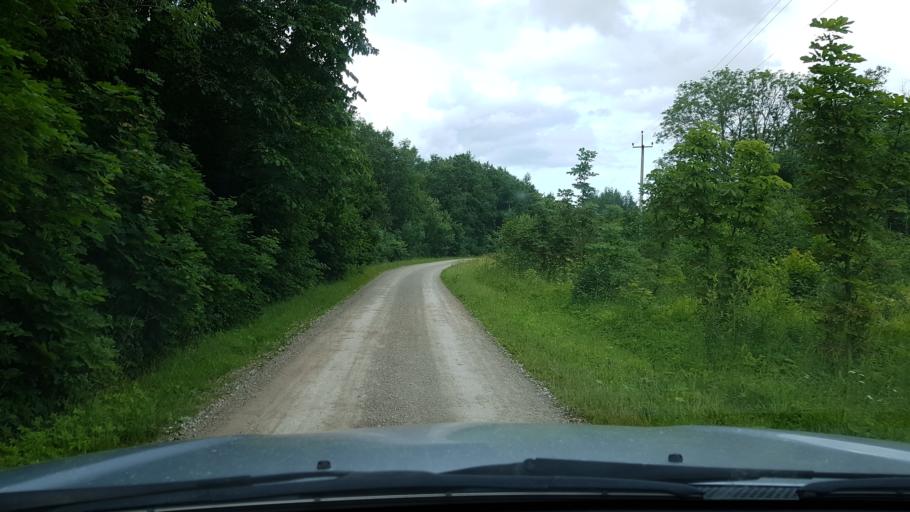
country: EE
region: Ida-Virumaa
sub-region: Narva-Joesuu linn
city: Narva-Joesuu
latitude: 59.4082
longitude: 27.9815
